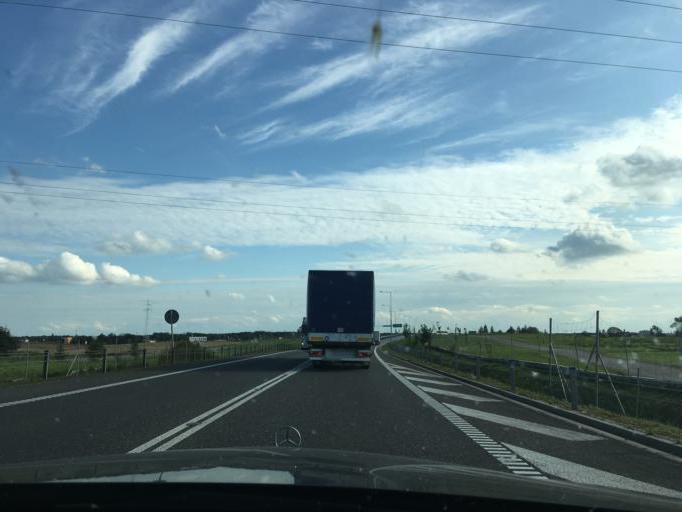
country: PL
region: Podlasie
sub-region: Powiat augustowski
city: Augustow
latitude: 53.8382
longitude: 22.9555
